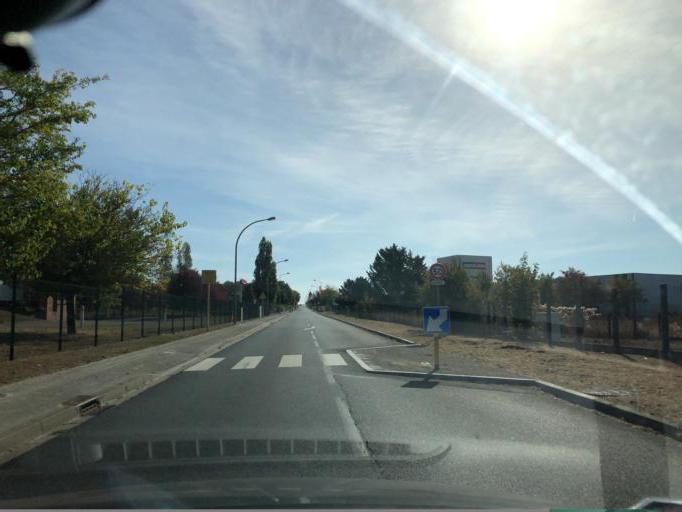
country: FR
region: Centre
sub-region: Departement du Loiret
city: Malesherbes
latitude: 48.2991
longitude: 2.3835
